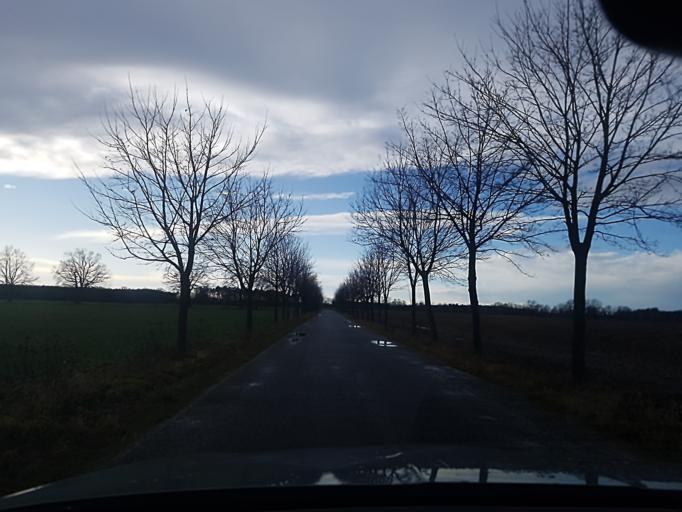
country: DE
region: Brandenburg
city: Falkenberg
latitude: 51.6106
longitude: 13.2927
